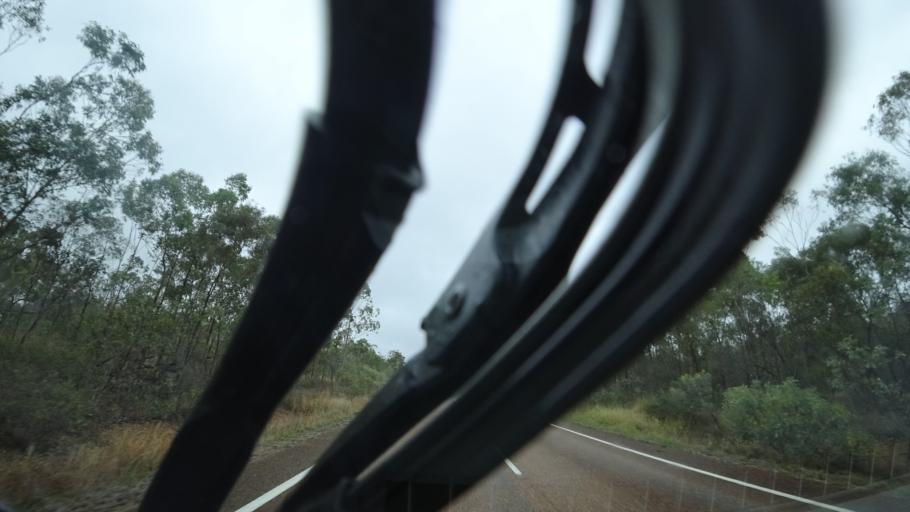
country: AU
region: Queensland
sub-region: Tablelands
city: Ravenshoe
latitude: -17.6902
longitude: 145.1514
